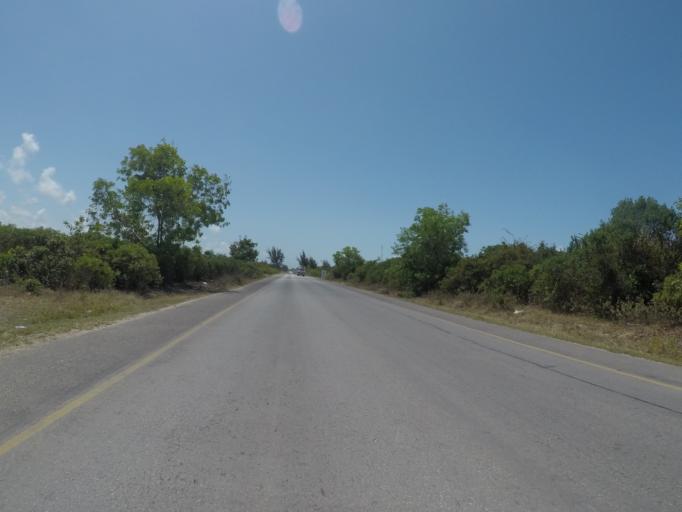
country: TZ
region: Zanzibar Central/South
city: Nganane
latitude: -6.3028
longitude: 39.5388
